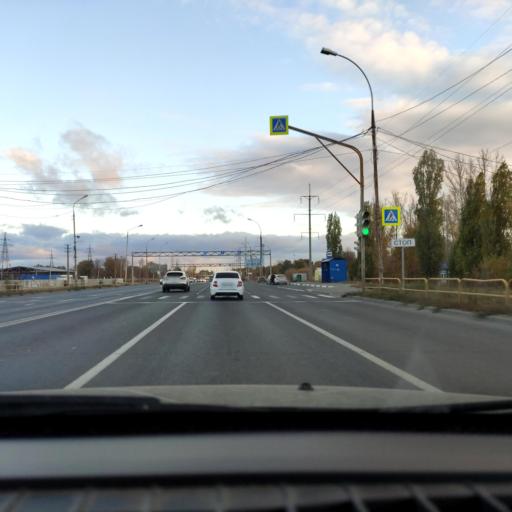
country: RU
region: Samara
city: Tol'yatti
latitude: 53.5626
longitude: 49.2900
